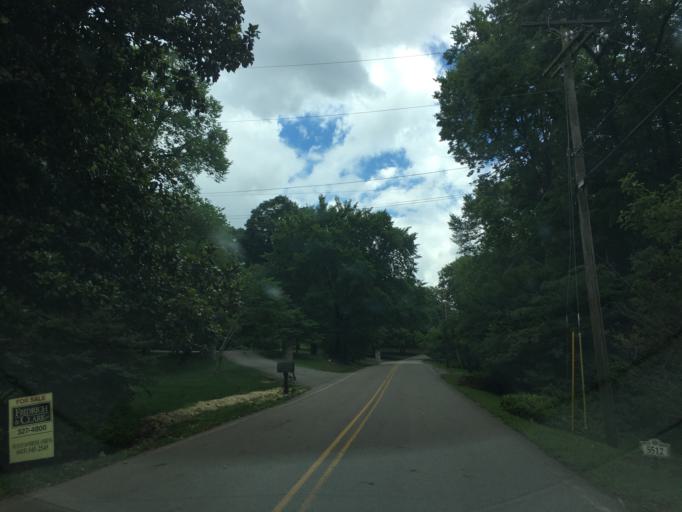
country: US
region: Tennessee
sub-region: Davidson County
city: Forest Hills
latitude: 36.0822
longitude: -86.8312
